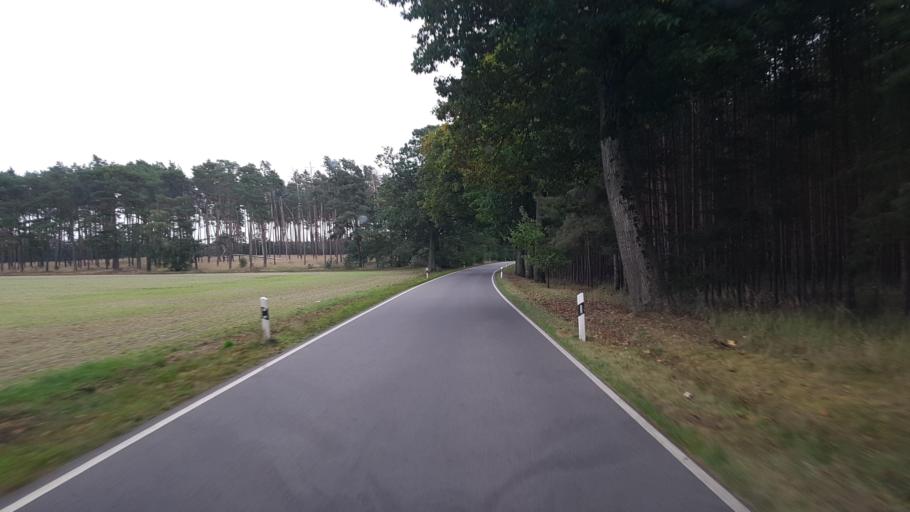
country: DE
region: Brandenburg
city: Kasel-Golzig
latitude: 51.8899
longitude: 13.6567
